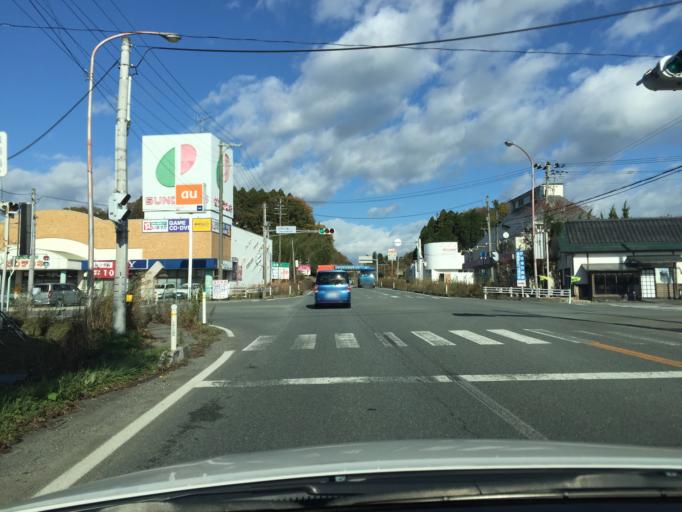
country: JP
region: Fukushima
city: Namie
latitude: 37.3428
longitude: 141.0127
